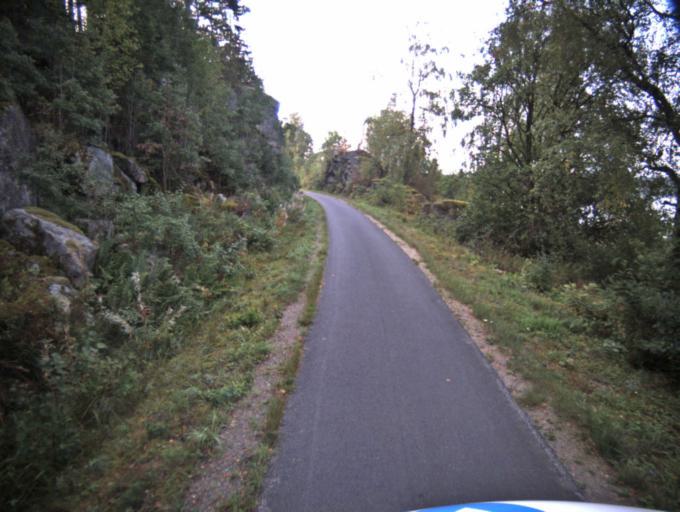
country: SE
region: Vaestra Goetaland
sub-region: Ulricehamns Kommun
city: Ulricehamn
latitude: 57.7037
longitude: 13.3941
